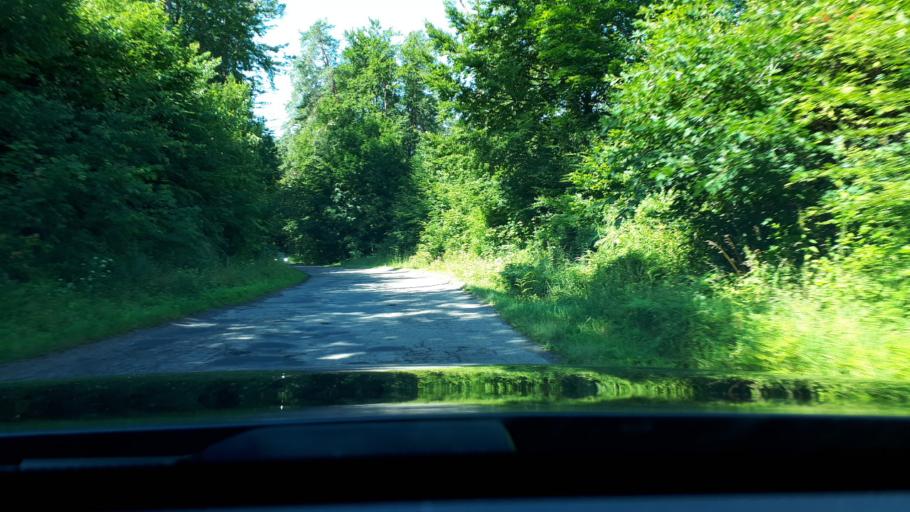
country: PL
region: Warmian-Masurian Voivodeship
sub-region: Powiat ostrodzki
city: Gierzwald
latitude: 53.6404
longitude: 20.0915
